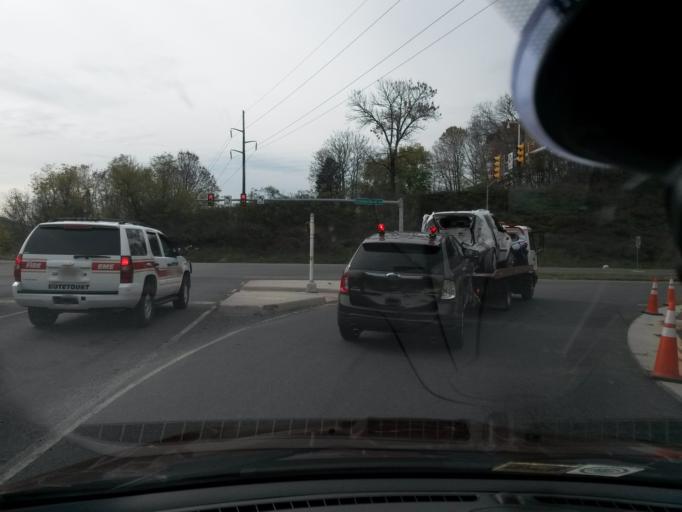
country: US
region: Virginia
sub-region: Botetourt County
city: Cloverdale
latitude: 37.3852
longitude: -79.8974
